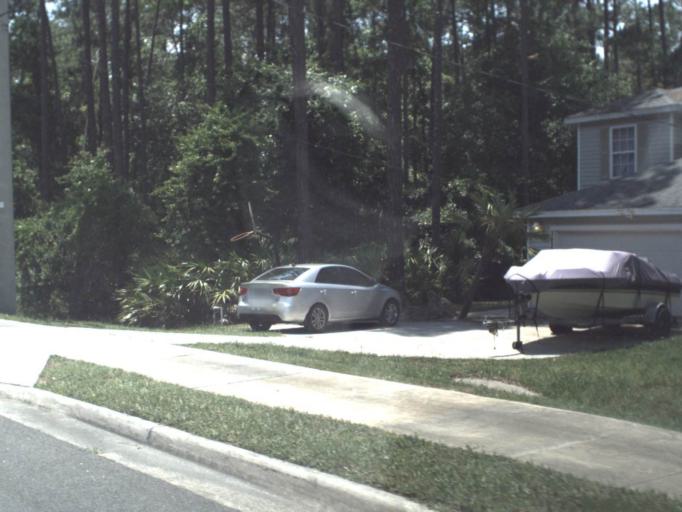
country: US
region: Florida
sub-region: Saint Johns County
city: Saint Augustine Shores
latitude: 29.8091
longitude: -81.4000
